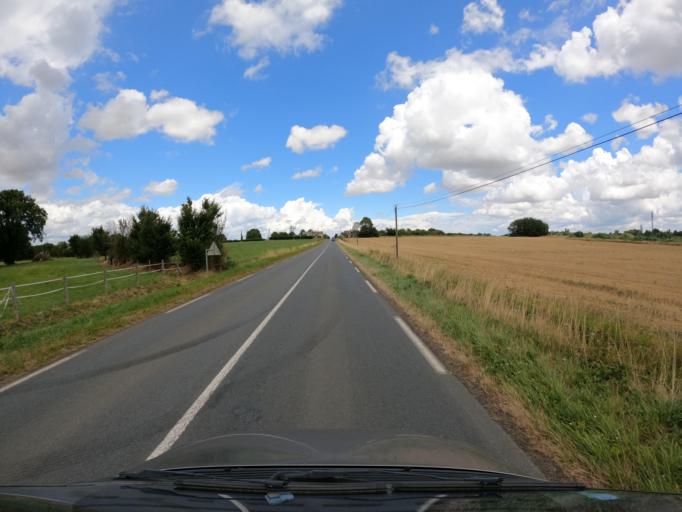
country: FR
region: Pays de la Loire
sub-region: Departement de la Sarthe
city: Solesmes
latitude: 47.8591
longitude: -0.3193
